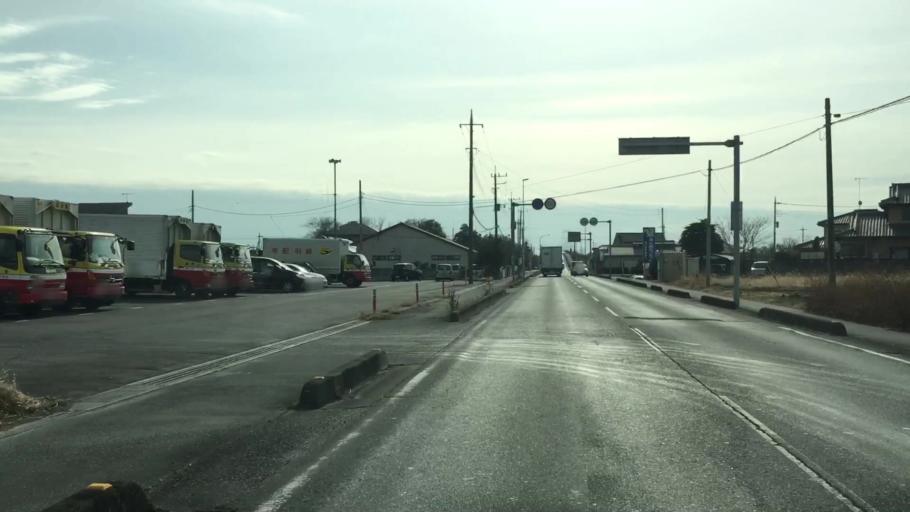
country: JP
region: Saitama
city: Fukayacho
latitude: 36.1486
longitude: 139.3227
